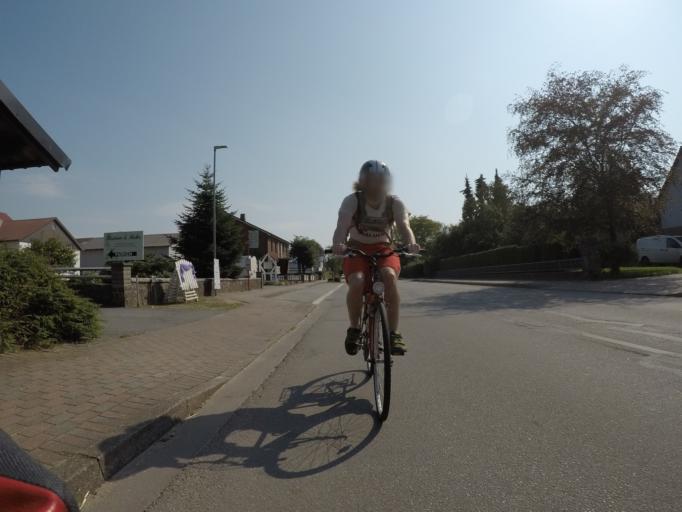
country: DE
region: Schleswig-Holstein
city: Todesfelde
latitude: 53.8936
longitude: 10.1761
